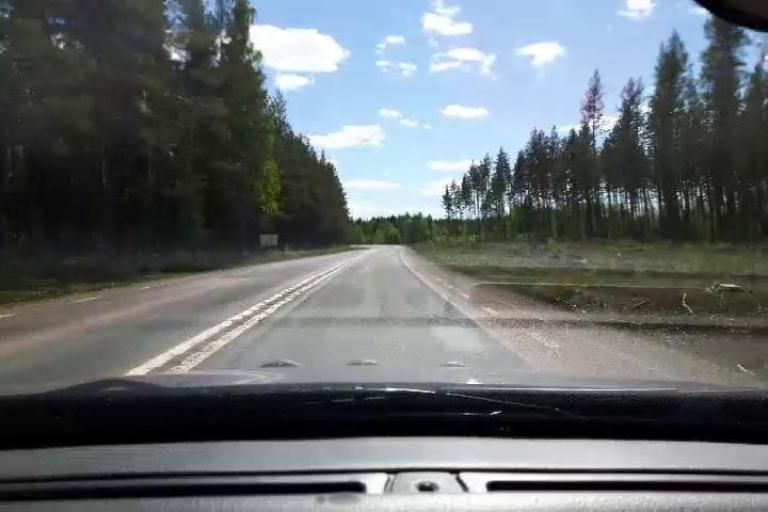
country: SE
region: Gaevleborg
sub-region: Ljusdals Kommun
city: Farila
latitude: 61.8363
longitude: 15.7513
